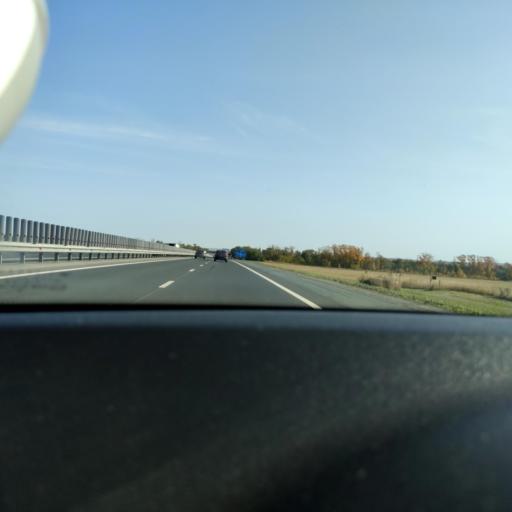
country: RU
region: Samara
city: Bereza
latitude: 53.4690
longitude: 50.1781
